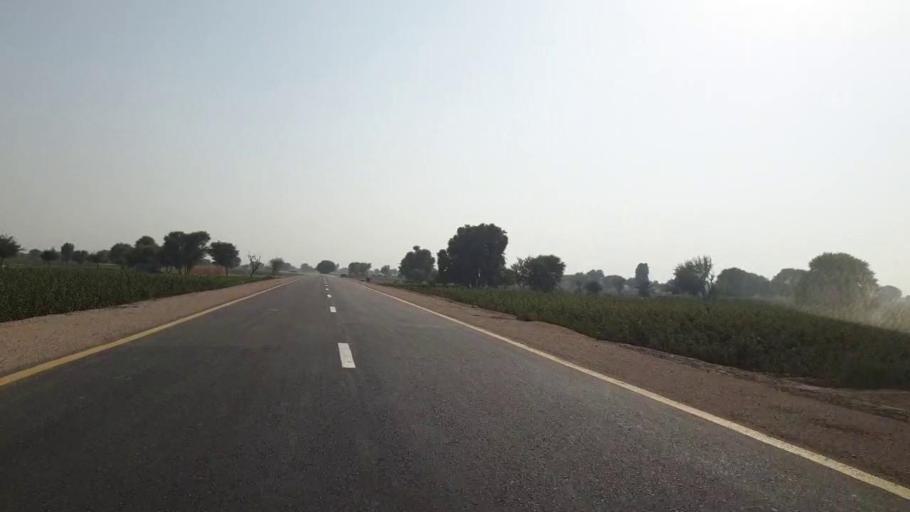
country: PK
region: Sindh
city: Bhan
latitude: 26.5113
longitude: 67.7850
